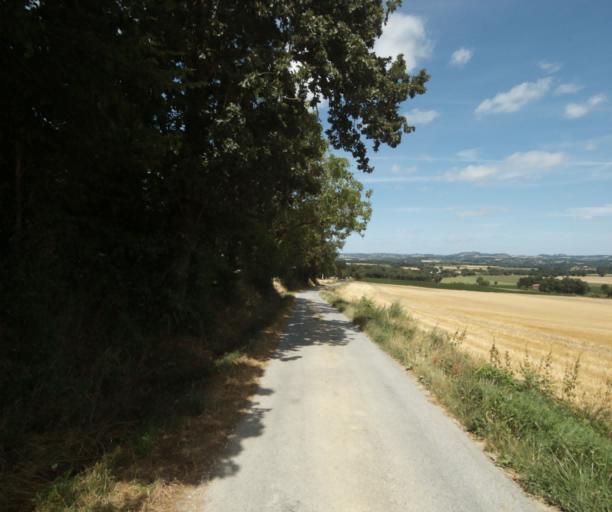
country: FR
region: Midi-Pyrenees
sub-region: Departement du Tarn
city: Soreze
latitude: 43.4919
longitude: 2.0684
